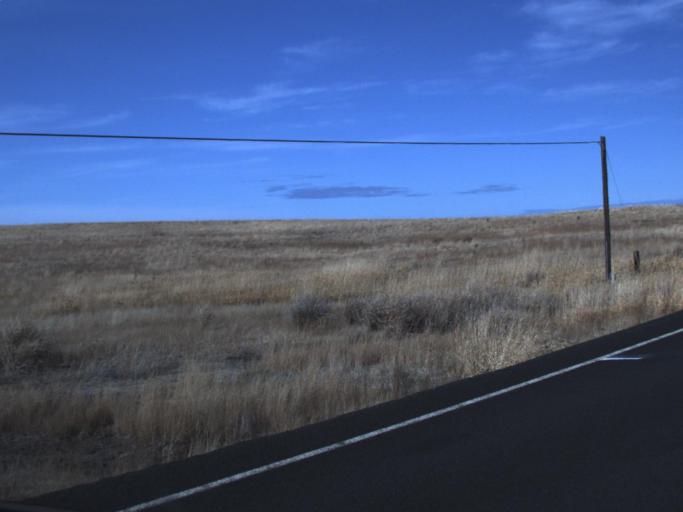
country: US
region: Washington
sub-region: Lincoln County
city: Davenport
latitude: 47.7604
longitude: -118.1735
